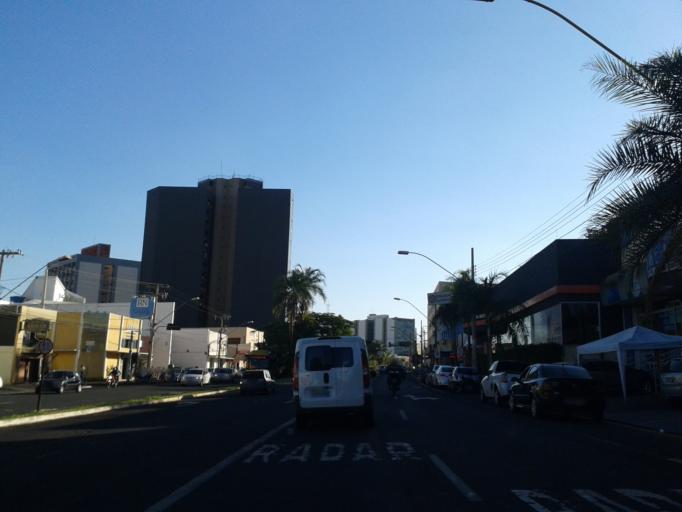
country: BR
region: Minas Gerais
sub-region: Uberlandia
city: Uberlandia
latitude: -18.9161
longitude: -48.2708
